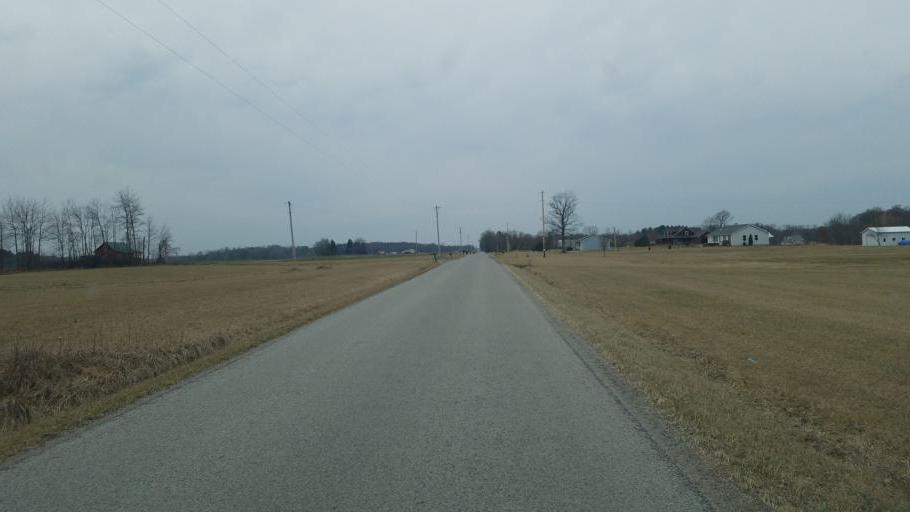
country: US
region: Ohio
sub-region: Morrow County
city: Mount Gilead
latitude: 40.6249
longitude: -82.7925
